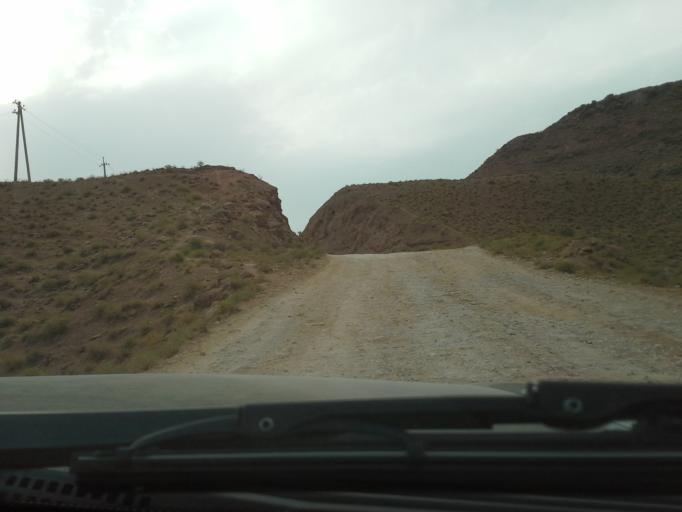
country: UZ
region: Qashqadaryo
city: Qorashina
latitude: 37.9382
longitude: 66.5265
